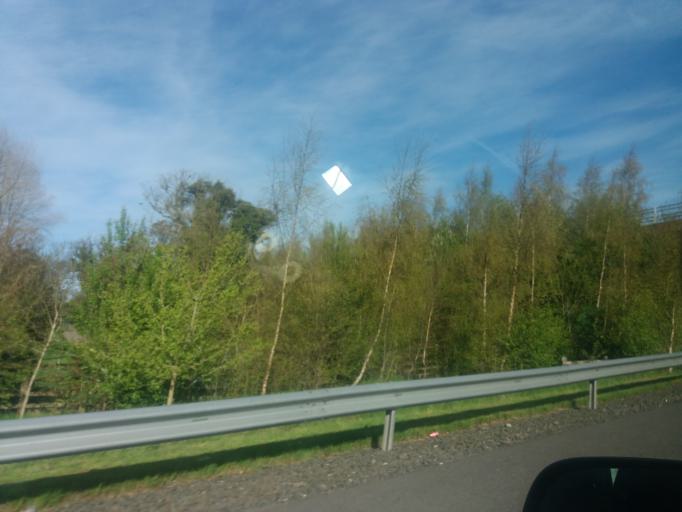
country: IE
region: Leinster
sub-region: An Mhi
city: Navan
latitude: 53.6630
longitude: -6.7590
